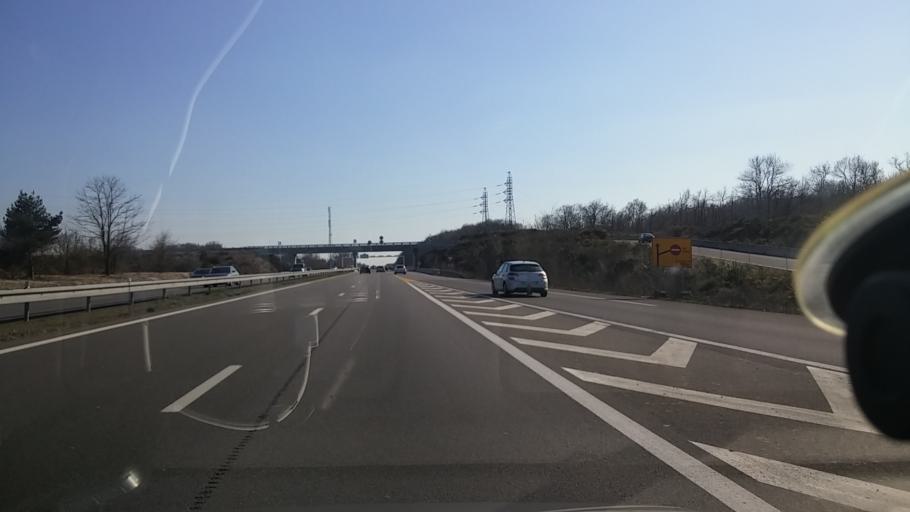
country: FR
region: Centre
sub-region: Departement du Loir-et-Cher
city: Theillay
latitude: 47.2879
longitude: 2.0437
